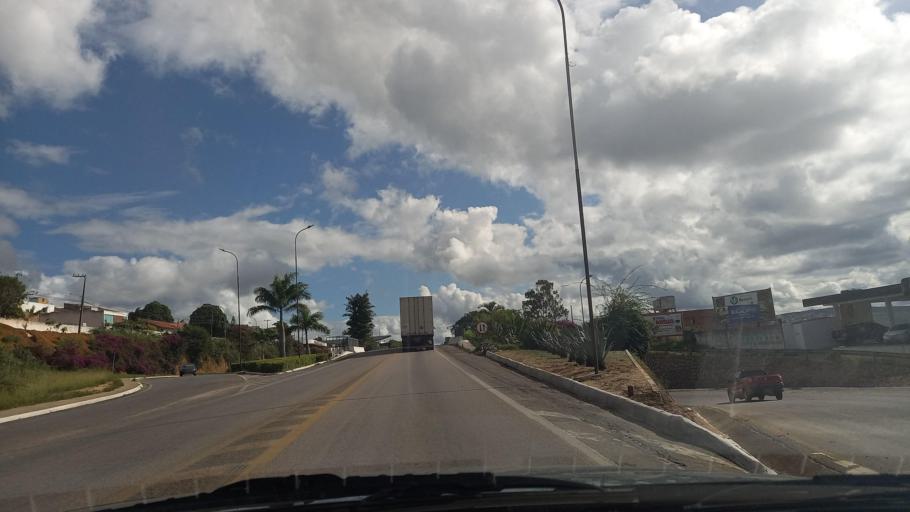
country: BR
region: Pernambuco
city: Garanhuns
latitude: -8.8758
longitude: -36.4723
